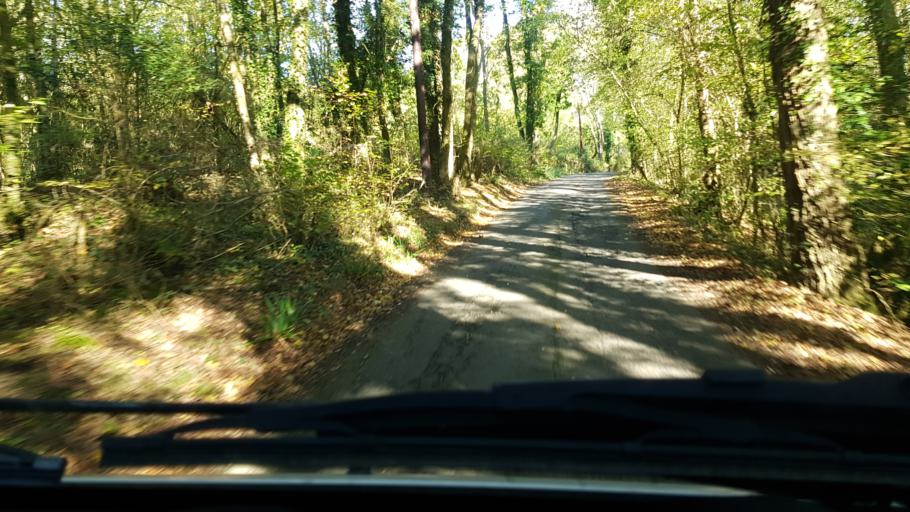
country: GB
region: England
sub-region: Surrey
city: Ockley
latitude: 51.1355
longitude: -0.3463
